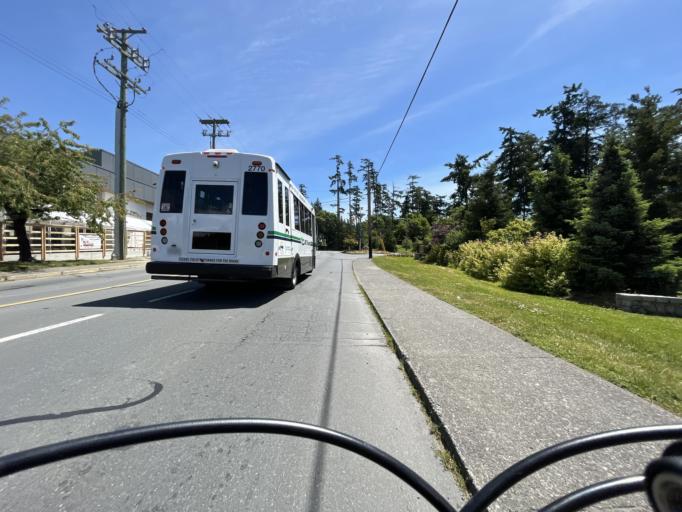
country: CA
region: British Columbia
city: Victoria
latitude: 48.4478
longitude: -123.4013
